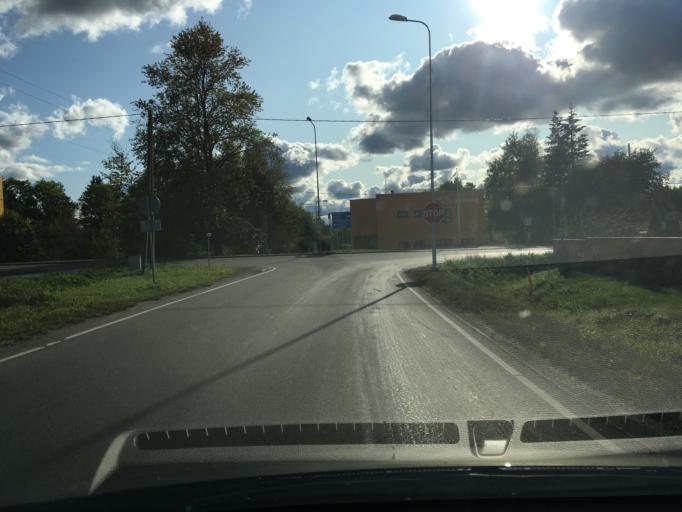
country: EE
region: Harju
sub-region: Joelaehtme vald
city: Loo
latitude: 59.4027
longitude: 24.9425
